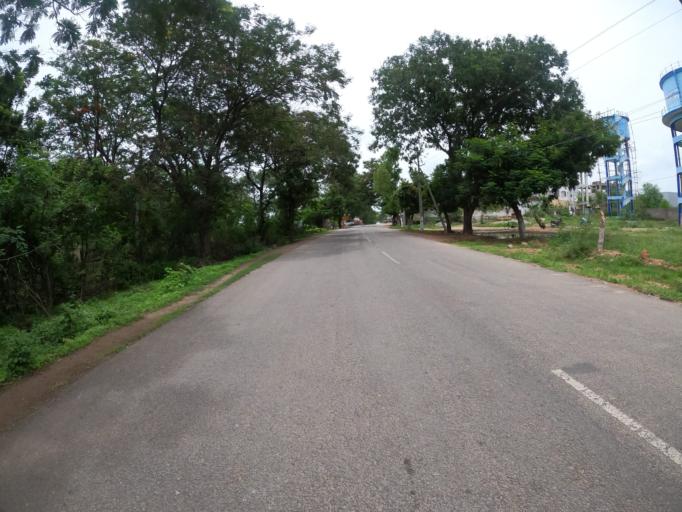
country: IN
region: Telangana
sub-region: Hyderabad
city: Hyderabad
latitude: 17.3410
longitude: 78.3610
